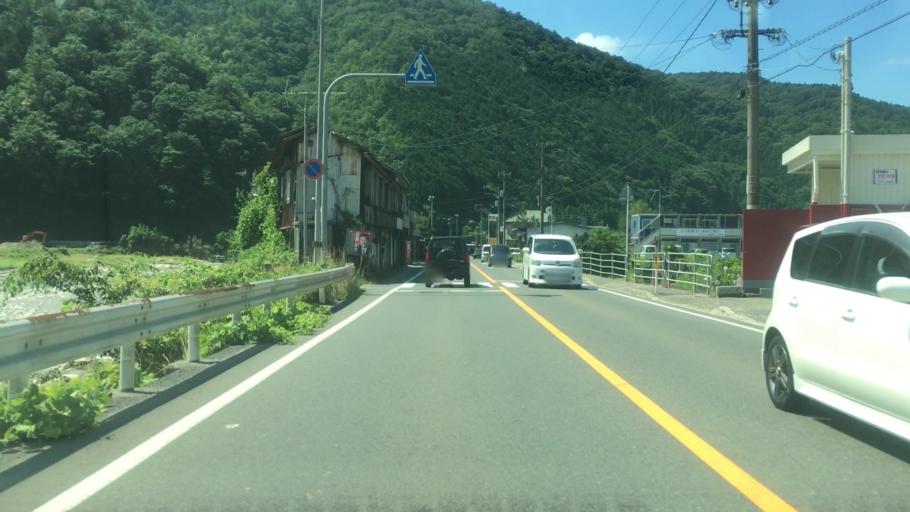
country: JP
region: Tottori
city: Tottori
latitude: 35.2710
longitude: 134.2262
